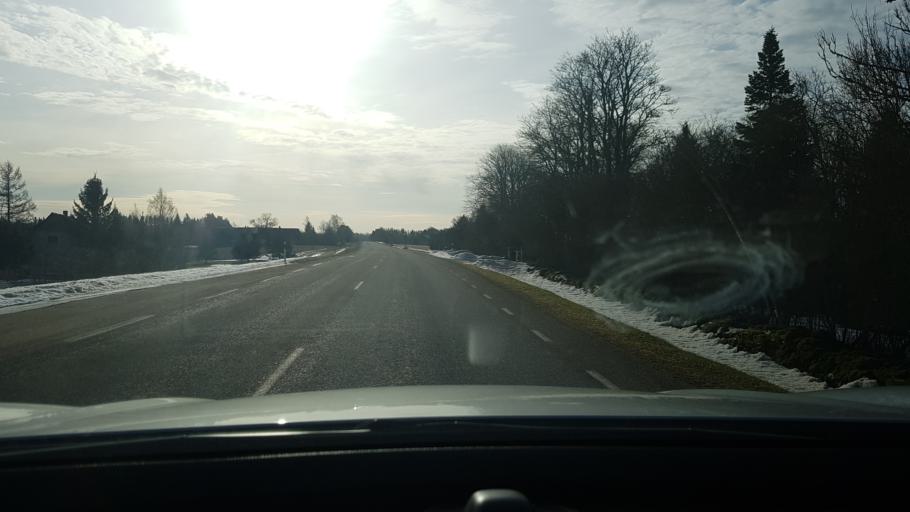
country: EE
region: Saare
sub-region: Kuressaare linn
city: Kuressaare
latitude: 58.5224
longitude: 22.7015
